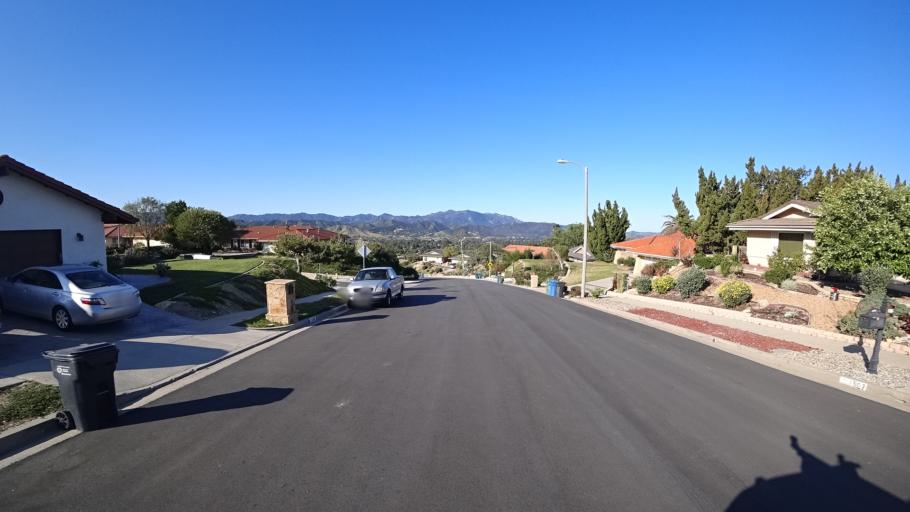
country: US
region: California
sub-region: Ventura County
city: Thousand Oaks
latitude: 34.1983
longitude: -118.8384
